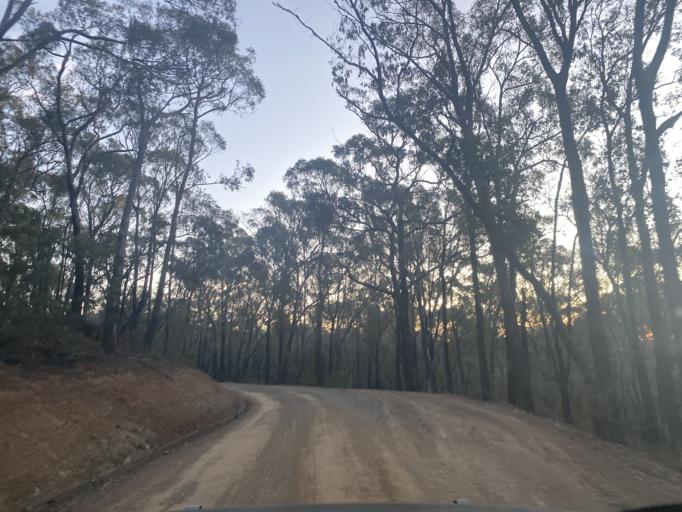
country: AU
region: Victoria
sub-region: Yarra Ranges
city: Healesville
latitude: -37.4445
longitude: 145.4862
